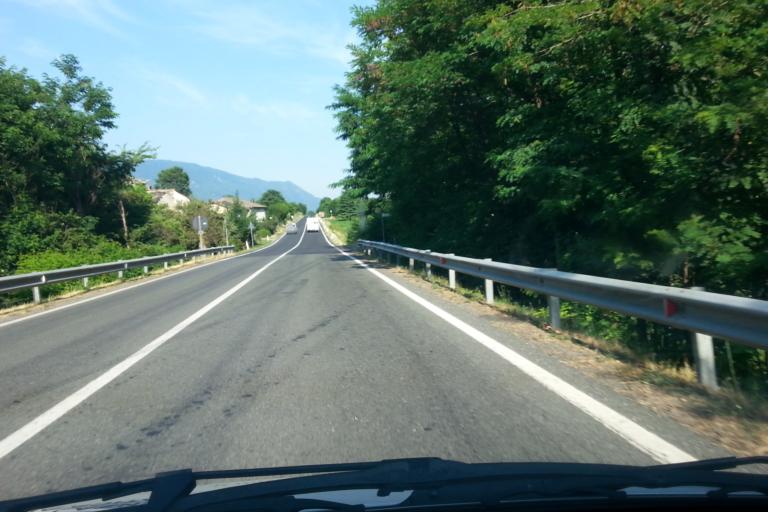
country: IT
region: Piedmont
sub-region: Provincia di Torino
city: Mattie
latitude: 45.1369
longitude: 7.1085
